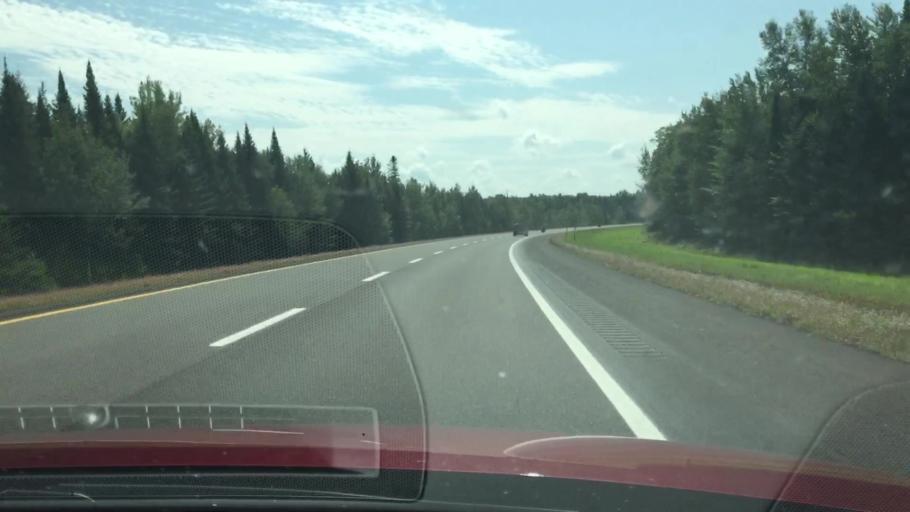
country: US
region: Maine
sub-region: Penobscot County
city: Patten
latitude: 45.9953
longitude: -68.2795
